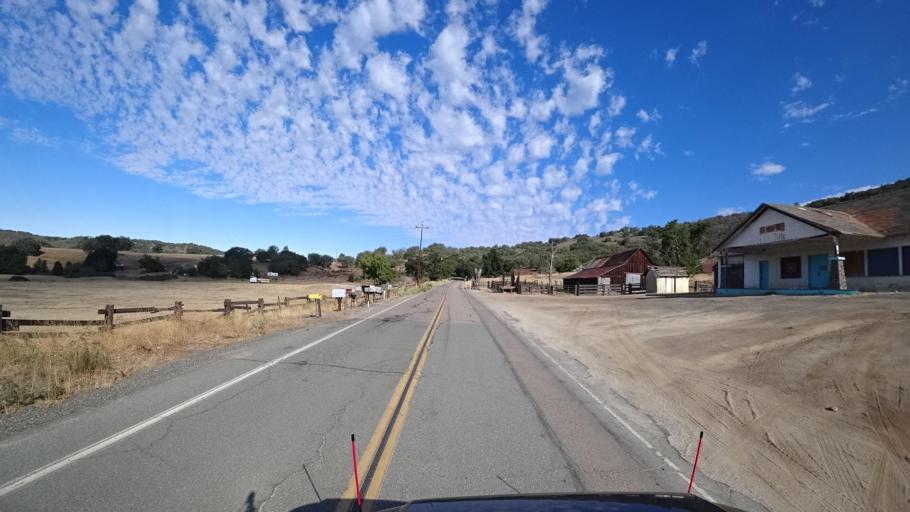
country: US
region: California
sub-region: San Diego County
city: Ramona
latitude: 33.1803
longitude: -116.7697
